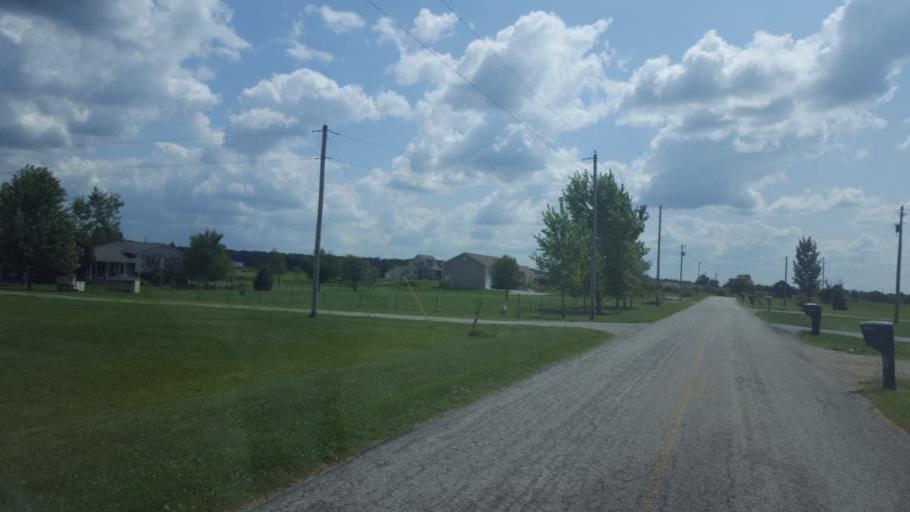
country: US
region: Ohio
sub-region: Delaware County
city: Ashley
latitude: 40.3432
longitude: -82.8798
